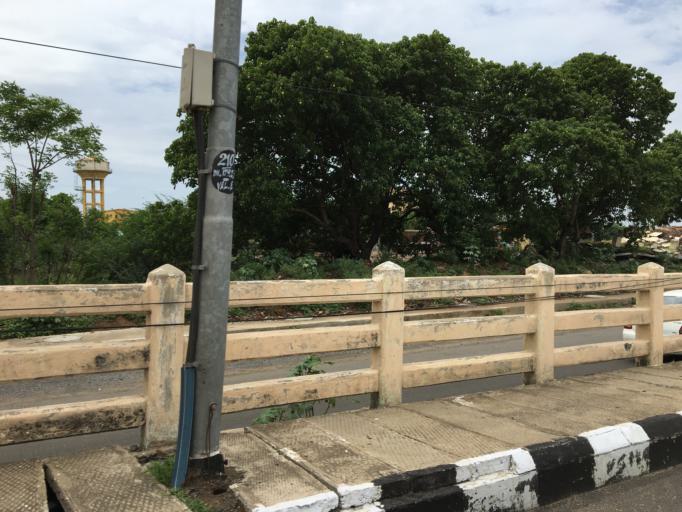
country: IN
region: Tamil Nadu
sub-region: Kancheepuram
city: Madipakkam
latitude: 12.9652
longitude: 80.2168
